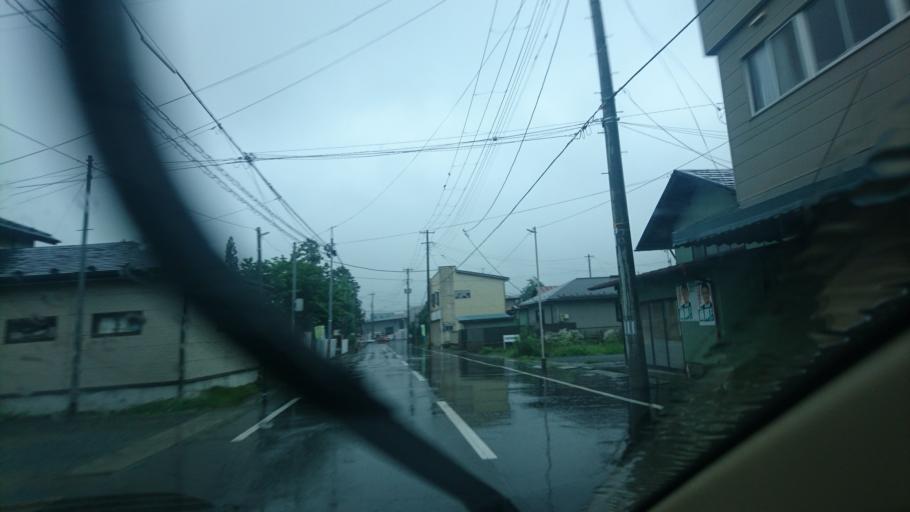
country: JP
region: Iwate
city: Mizusawa
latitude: 39.1885
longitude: 141.1803
